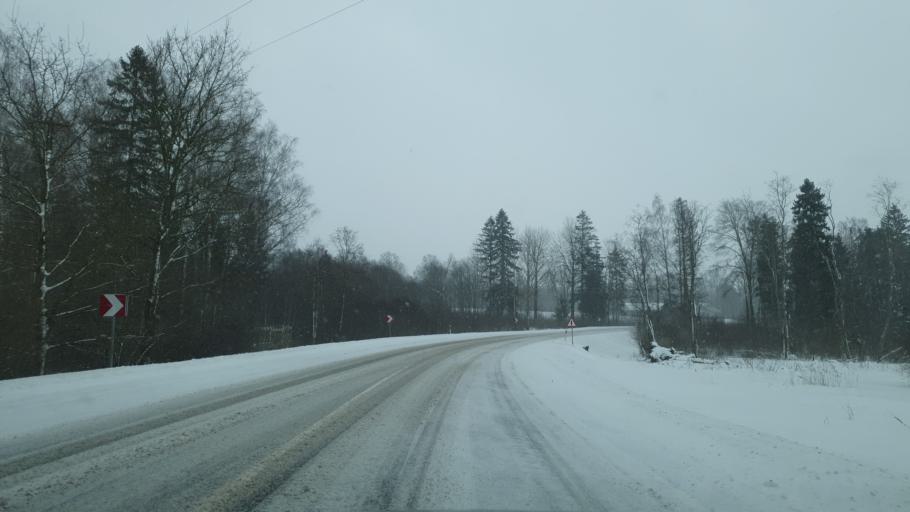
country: EE
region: Jaervamaa
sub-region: Jaerva-Jaani vald
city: Jarva-Jaani
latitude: 59.0606
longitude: 25.8741
